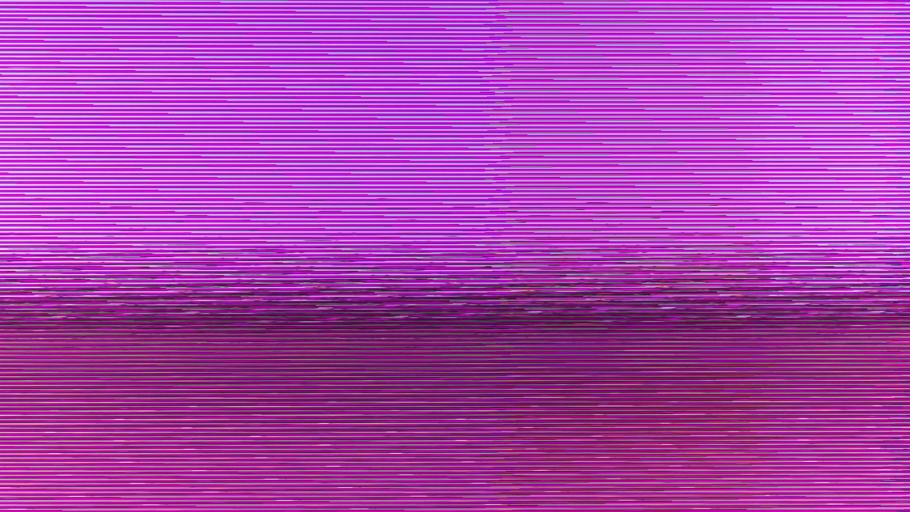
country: US
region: Michigan
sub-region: Wayne County
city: Belleville
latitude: 42.2193
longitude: -83.5445
